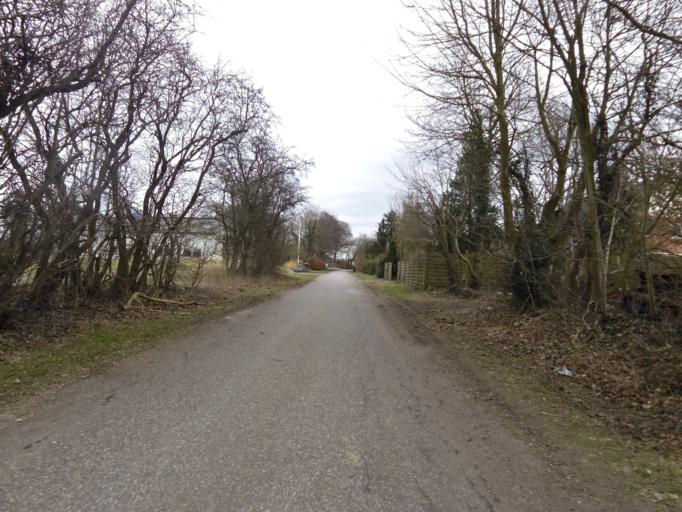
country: DK
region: South Denmark
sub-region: Tonder Kommune
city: Toftlund
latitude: 55.2083
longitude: 9.1769
